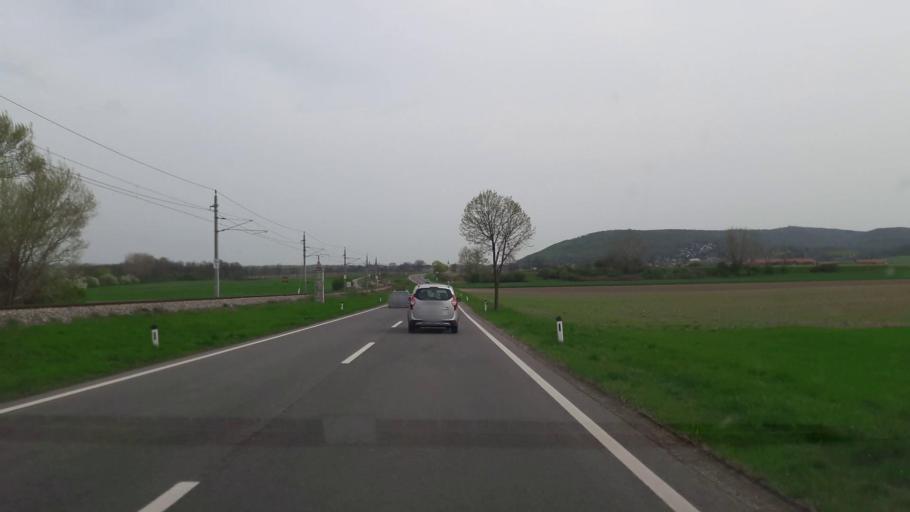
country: AT
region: Lower Austria
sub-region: Politischer Bezirk Bruck an der Leitha
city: Wolfsthal
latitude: 48.1427
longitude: 16.9827
